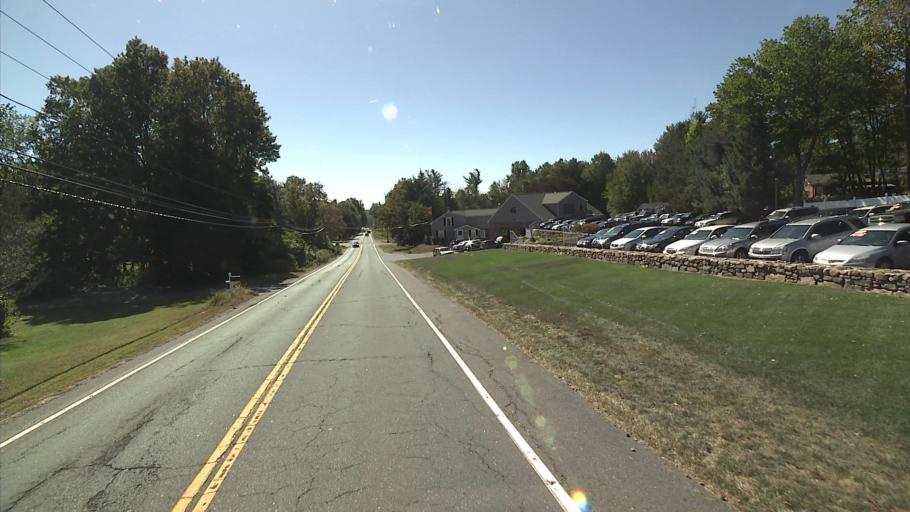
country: US
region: Connecticut
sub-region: New Haven County
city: Prospect
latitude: 41.4720
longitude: -72.9679
